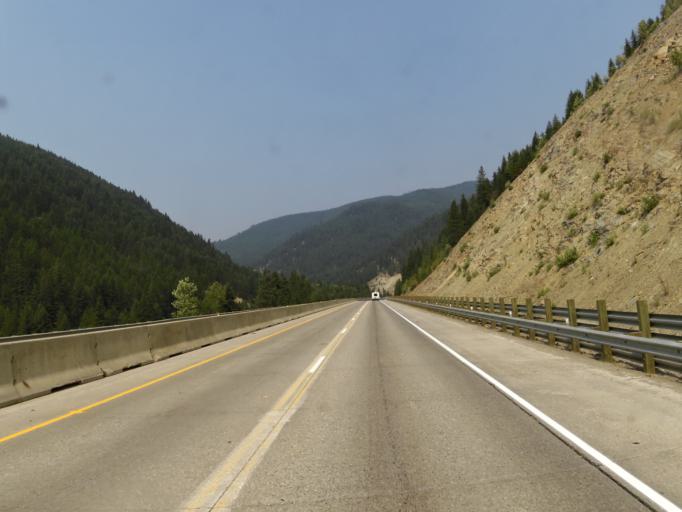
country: US
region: Montana
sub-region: Sanders County
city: Thompson Falls
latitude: 47.3058
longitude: -115.2046
